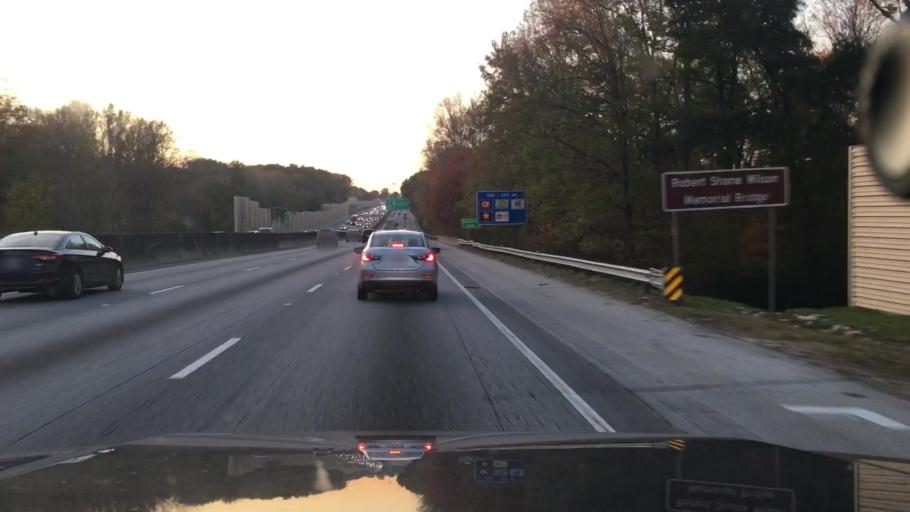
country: US
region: Georgia
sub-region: DeKalb County
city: Panthersville
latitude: 33.7043
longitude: -84.1960
